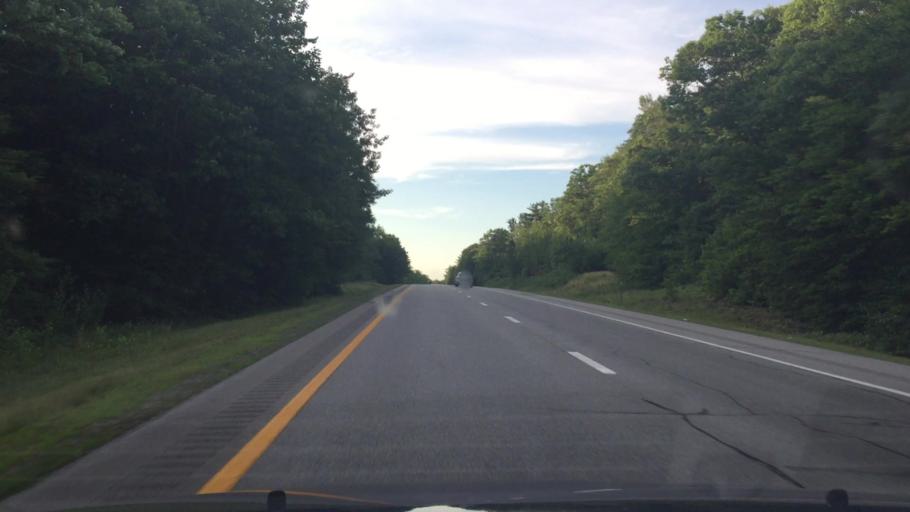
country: US
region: New Hampshire
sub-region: Belknap County
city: Sanbornton
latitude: 43.5428
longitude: -71.6153
